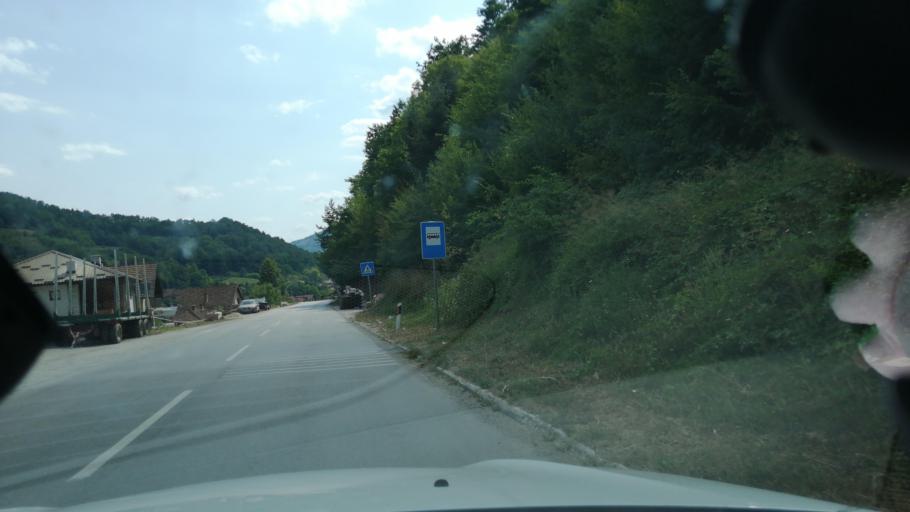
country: RS
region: Central Serbia
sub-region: Moravicki Okrug
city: Ivanjica
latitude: 43.6095
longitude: 20.2352
